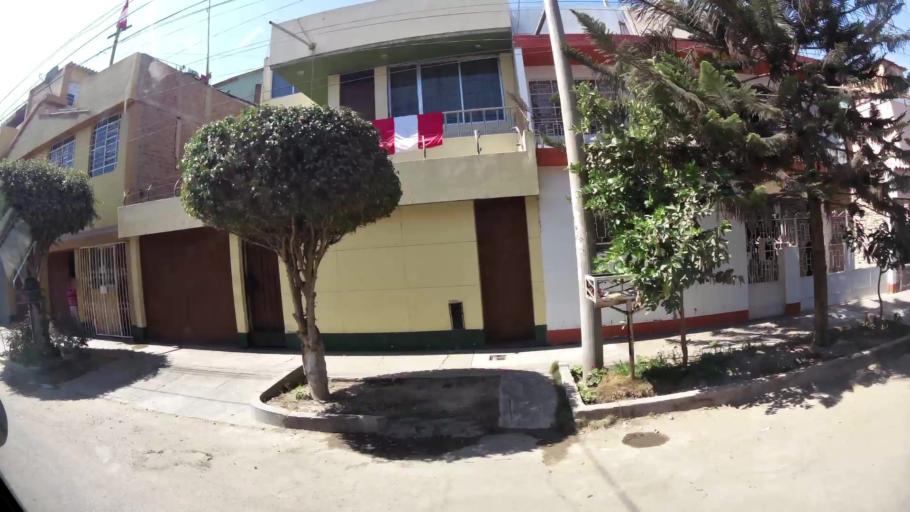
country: PE
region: Ica
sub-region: Provincia de Ica
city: Ica
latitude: -14.0720
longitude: -75.7317
